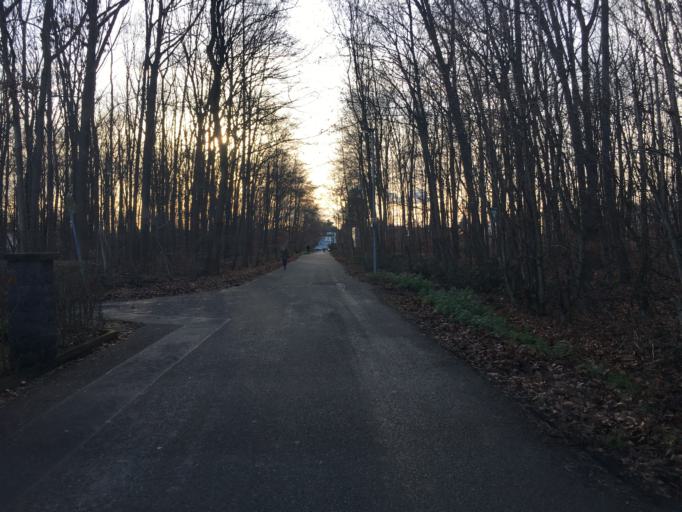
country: DE
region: North Rhine-Westphalia
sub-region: Regierungsbezirk Koln
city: Poll
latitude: 50.8847
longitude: 7.0144
